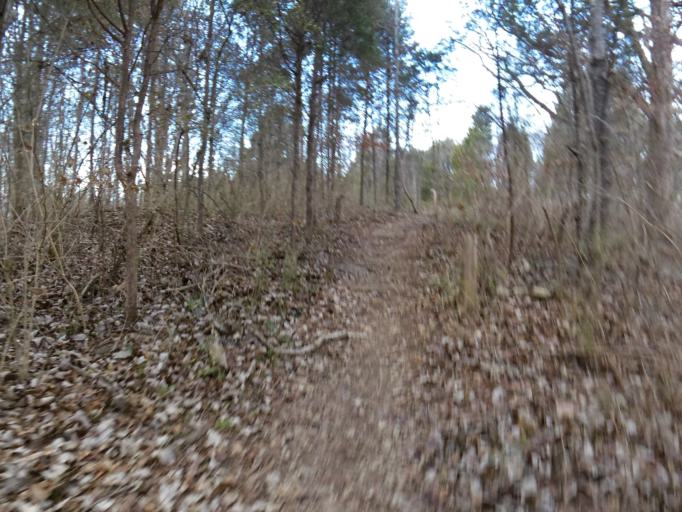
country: US
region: Tennessee
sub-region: Knox County
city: Knoxville
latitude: 35.9541
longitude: -83.8452
